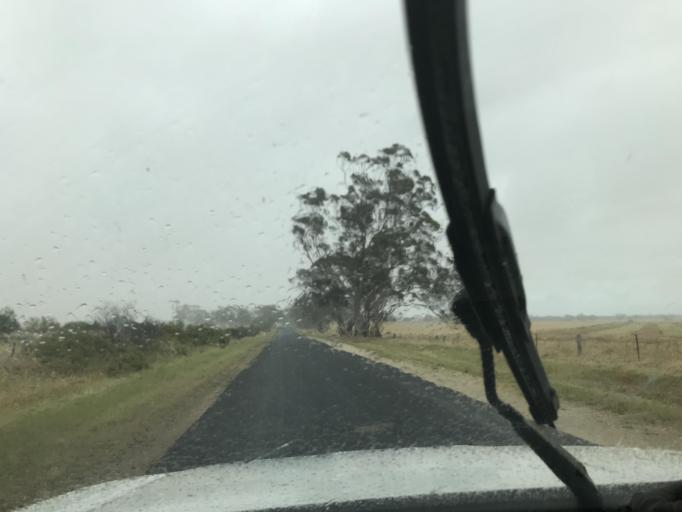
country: AU
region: South Australia
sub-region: Tatiara
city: Bordertown
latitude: -36.3286
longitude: 141.2113
